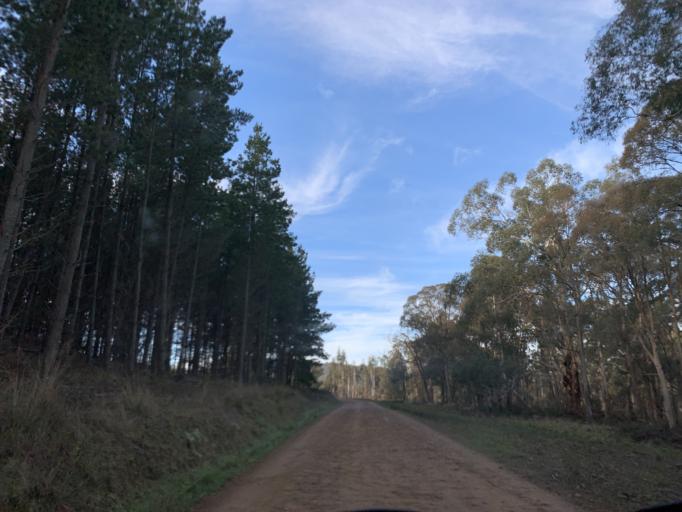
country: AU
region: Victoria
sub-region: Mansfield
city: Mansfield
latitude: -36.9232
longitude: 146.1013
